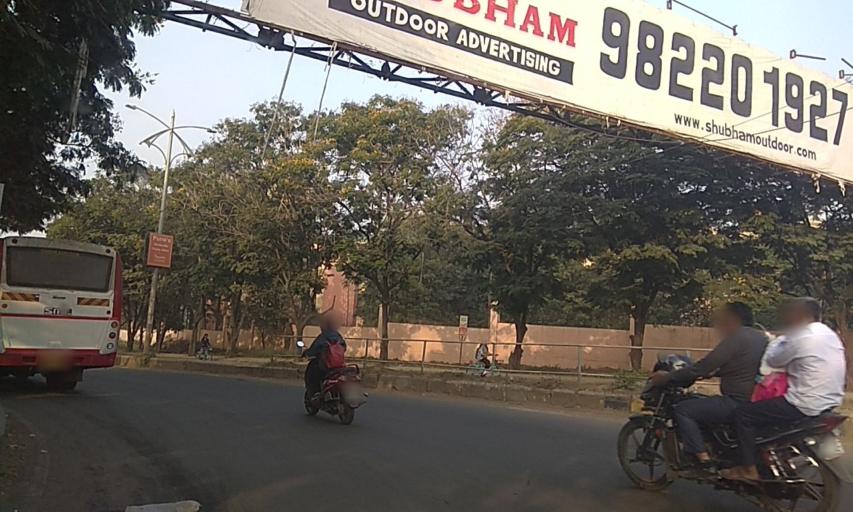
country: IN
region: Maharashtra
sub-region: Pune Division
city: Pimpri
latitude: 18.5857
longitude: 73.7332
